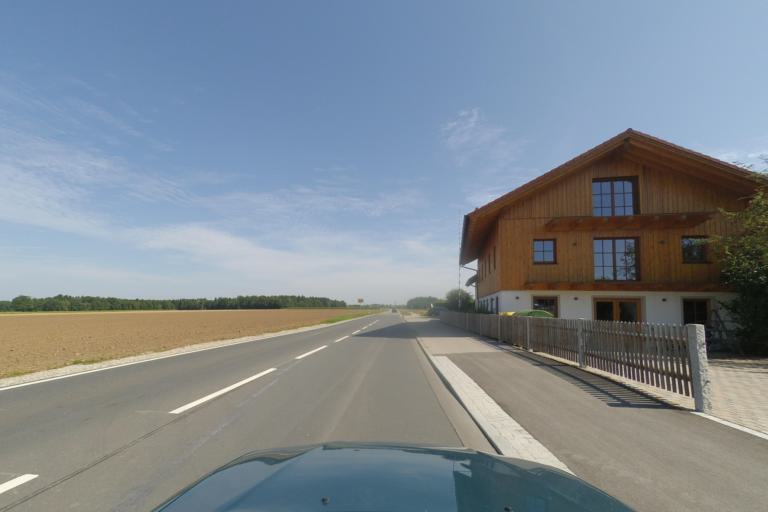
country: DE
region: Bavaria
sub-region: Upper Bavaria
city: Brunnthal
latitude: 48.0085
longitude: 11.6898
